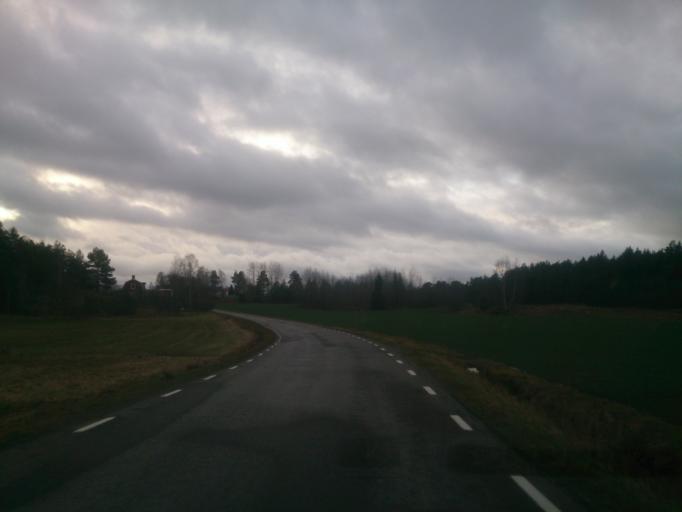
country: SE
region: OEstergoetland
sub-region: Norrkopings Kommun
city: Krokek
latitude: 58.5504
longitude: 16.6003
